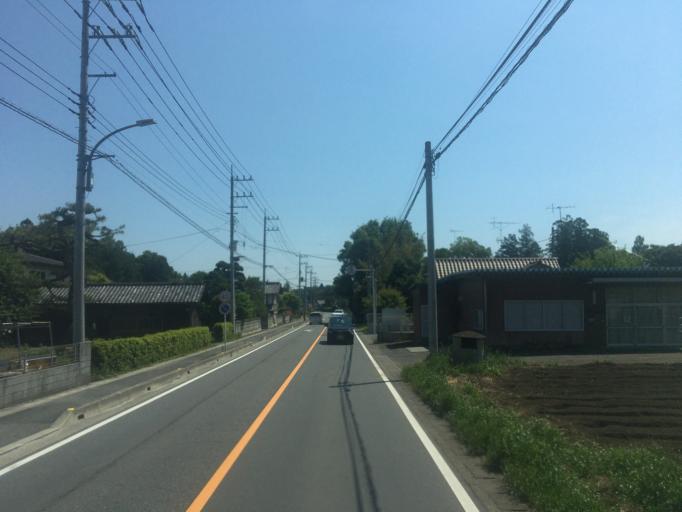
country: JP
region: Saitama
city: Ogawa
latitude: 36.0196
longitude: 139.3168
